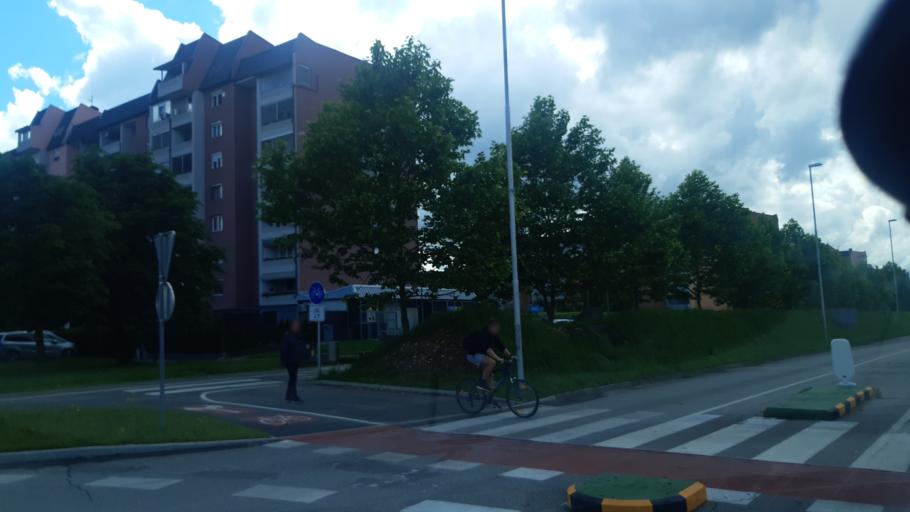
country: SI
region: Kranj
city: Kranj
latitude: 46.2385
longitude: 14.3703
